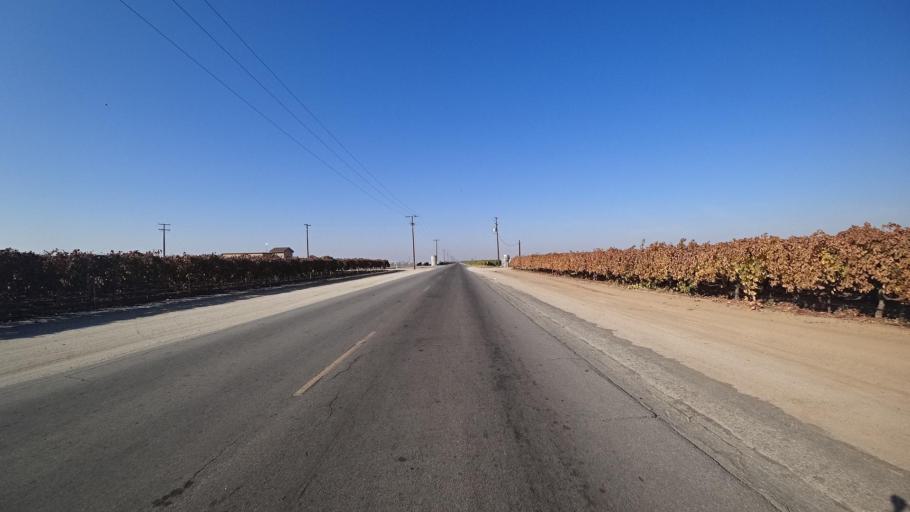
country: US
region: California
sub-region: Kern County
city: Delano
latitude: 35.7469
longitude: -119.1954
